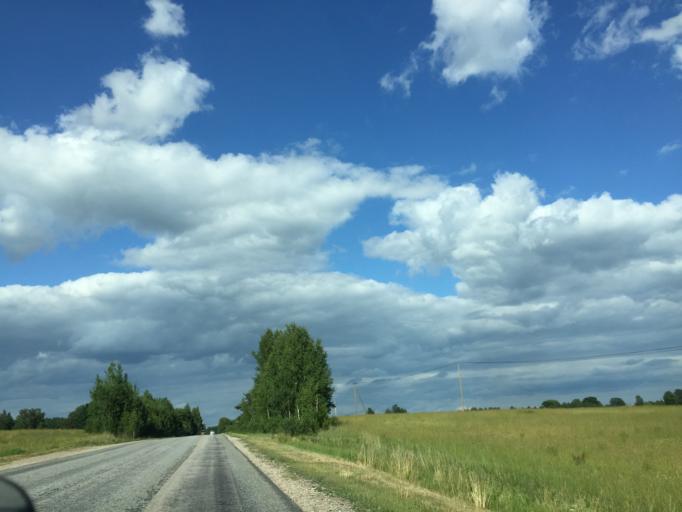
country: LV
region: Ogre
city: Jumprava
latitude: 56.7891
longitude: 25.0308
